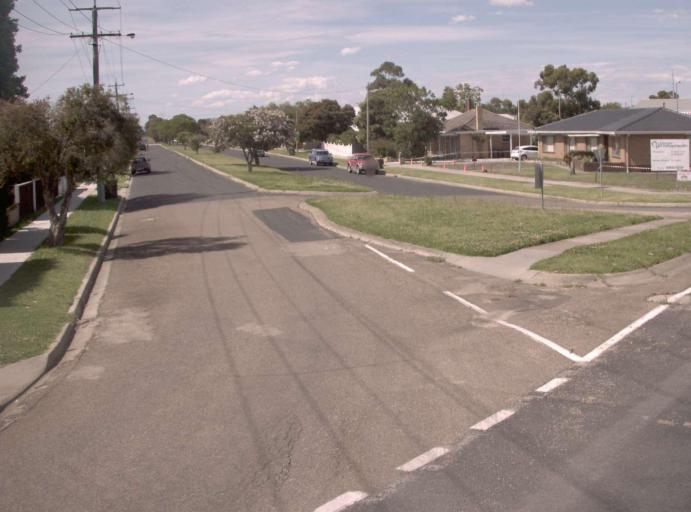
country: AU
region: Victoria
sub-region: East Gippsland
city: Bairnsdale
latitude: -37.8306
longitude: 147.6114
